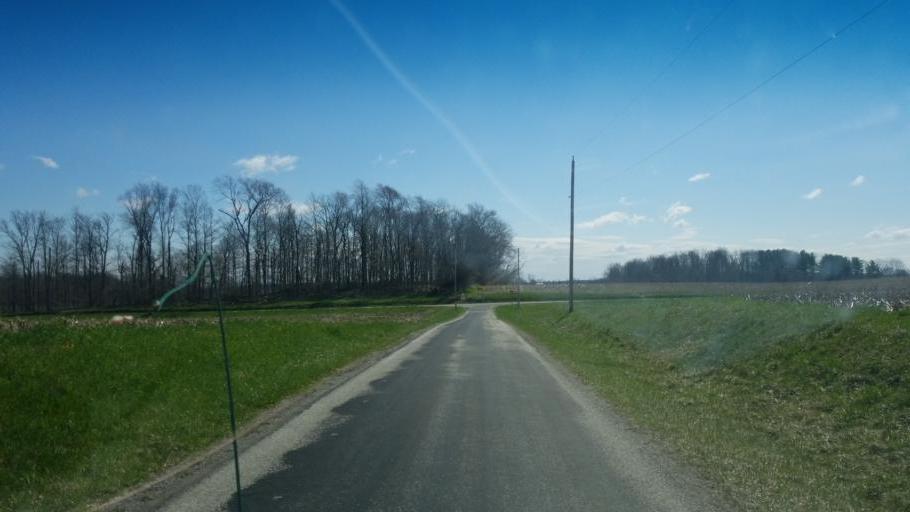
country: US
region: Ohio
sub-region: Crawford County
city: Crestline
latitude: 40.8798
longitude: -82.8380
